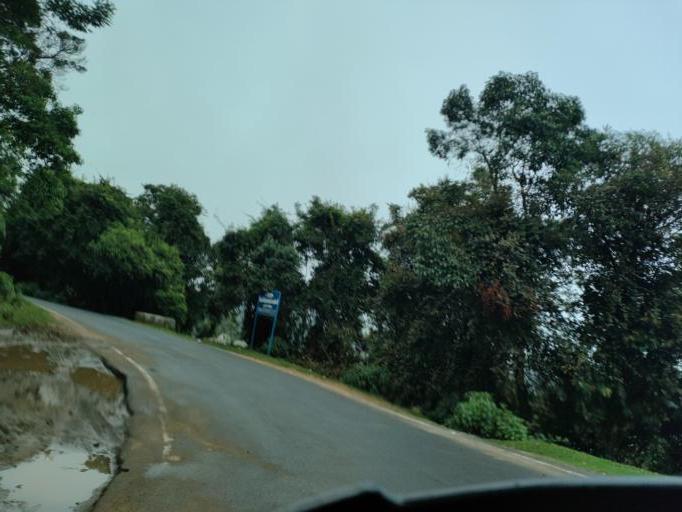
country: IN
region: Tamil Nadu
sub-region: Dindigul
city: Kodaikanal
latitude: 10.2520
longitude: 77.3958
